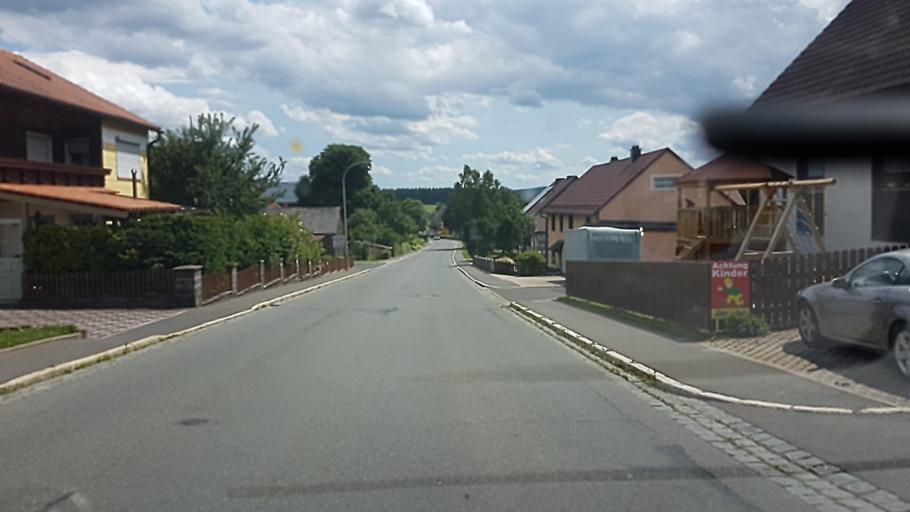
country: DE
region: Bavaria
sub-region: Upper Palatinate
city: Brand
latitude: 49.9627
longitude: 11.9070
